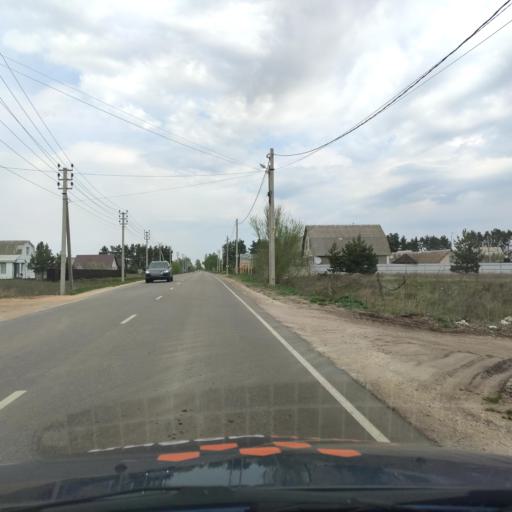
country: RU
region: Voronezj
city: Podgornoye
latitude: 51.8735
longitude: 39.1732
